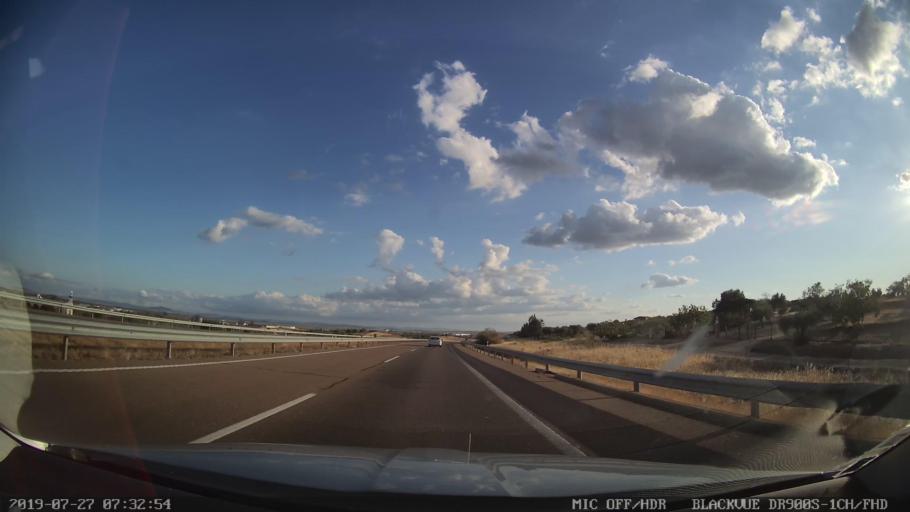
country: ES
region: Extremadura
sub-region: Provincia de Caceres
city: Miajadas
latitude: 39.1508
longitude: -5.9287
